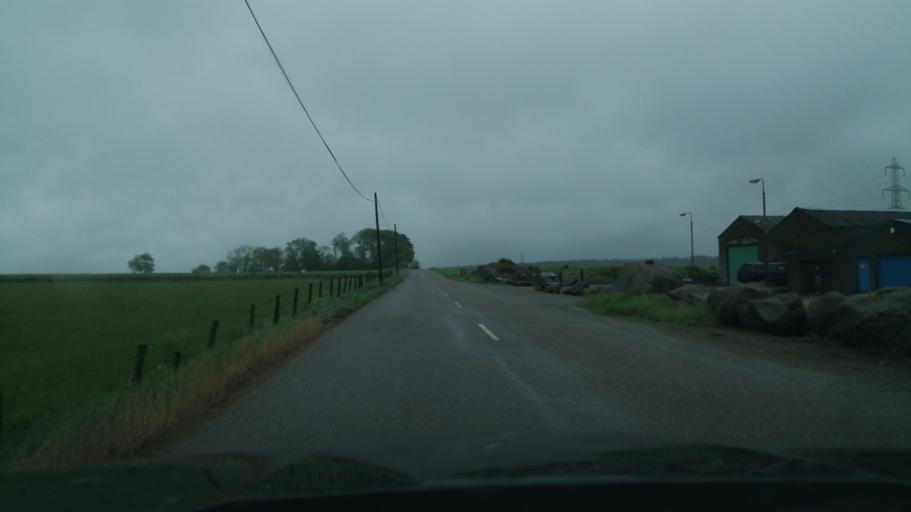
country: GB
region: Scotland
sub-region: Aberdeenshire
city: Huntly
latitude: 57.5477
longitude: -2.8194
